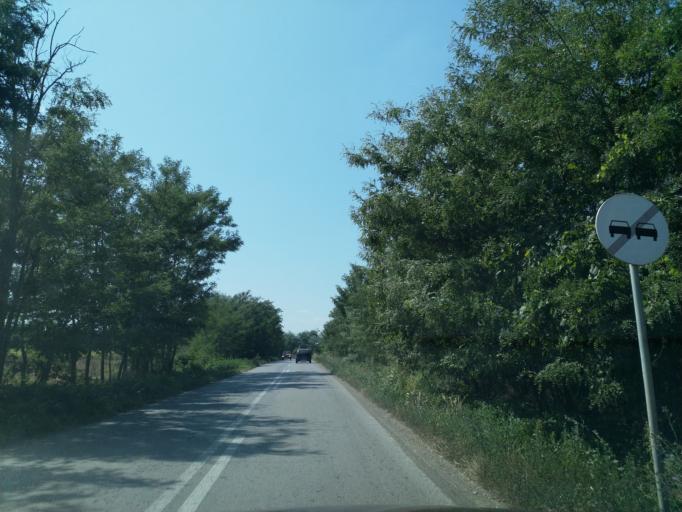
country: RS
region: Central Serbia
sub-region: Rasinski Okrug
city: Trstenik
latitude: 43.6292
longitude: 21.1519
